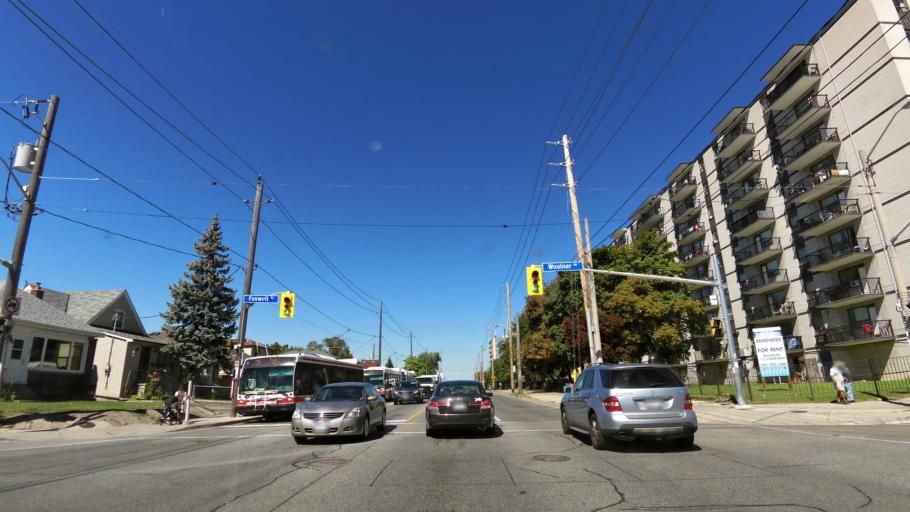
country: CA
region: Ontario
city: Etobicoke
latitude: 43.6716
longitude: -79.4937
